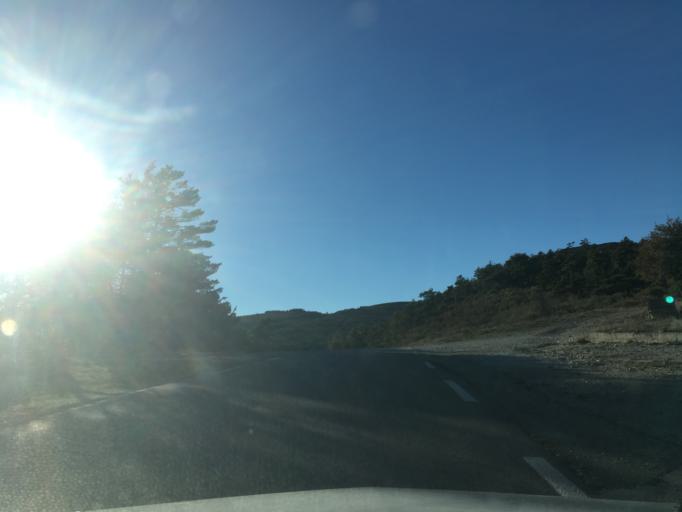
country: FR
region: Provence-Alpes-Cote d'Azur
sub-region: Departement des Alpes-de-Haute-Provence
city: Castellane
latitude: 43.7573
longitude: 6.4408
